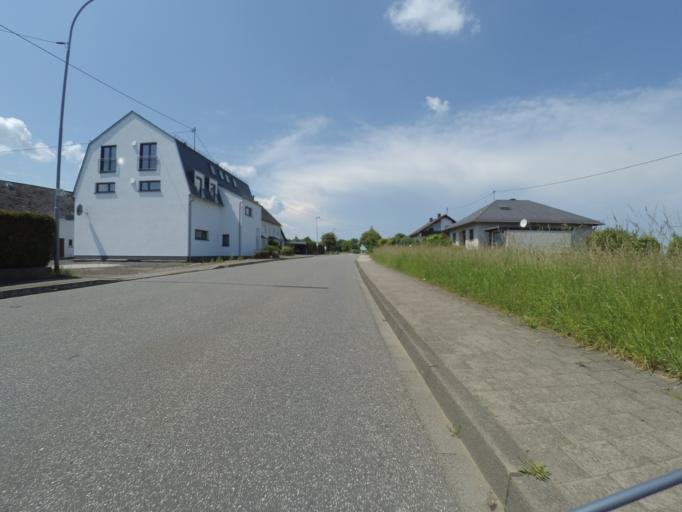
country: DE
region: Rheinland-Pfalz
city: Schwall
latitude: 50.1570
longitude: 7.5359
